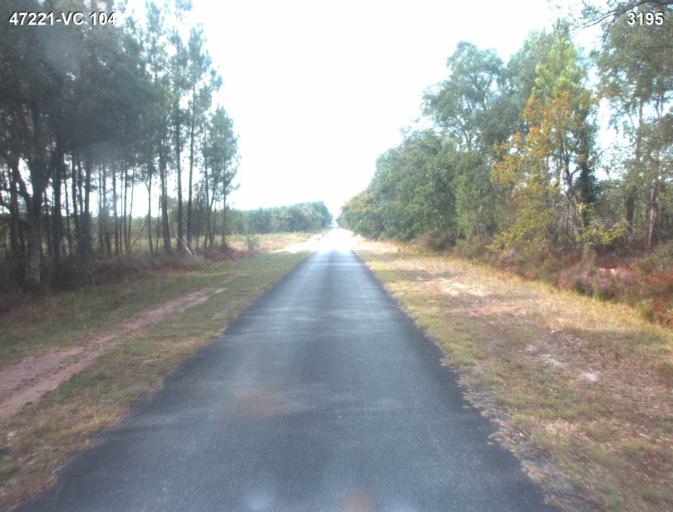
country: FR
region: Aquitaine
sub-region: Departement du Lot-et-Garonne
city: Mezin
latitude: 44.1240
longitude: 0.1891
